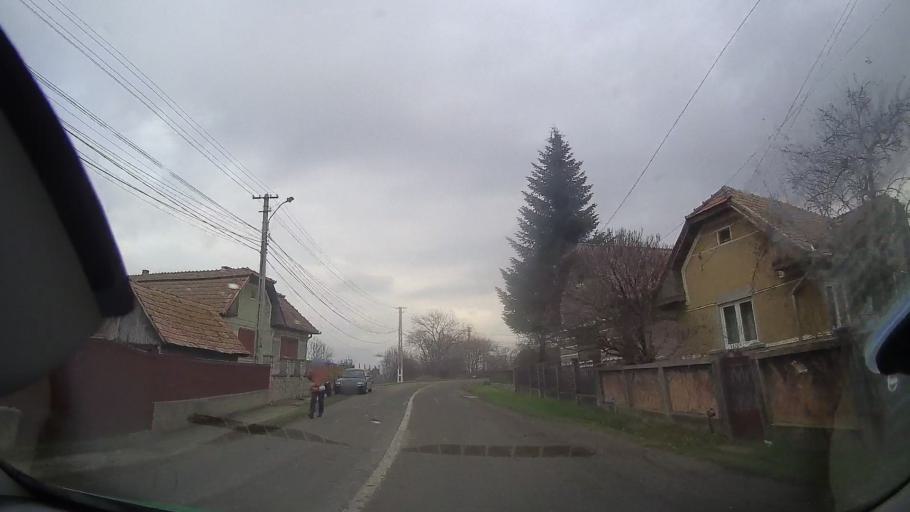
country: RO
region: Cluj
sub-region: Comuna Moldovenesti
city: Moldovenesti
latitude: 46.4994
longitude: 23.6705
